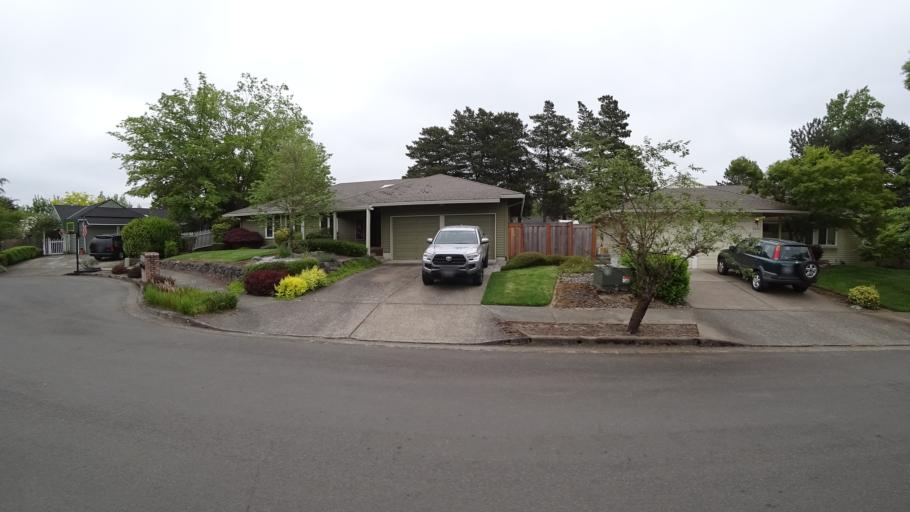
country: US
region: Oregon
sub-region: Washington County
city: Rockcreek
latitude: 45.5599
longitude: -122.8849
